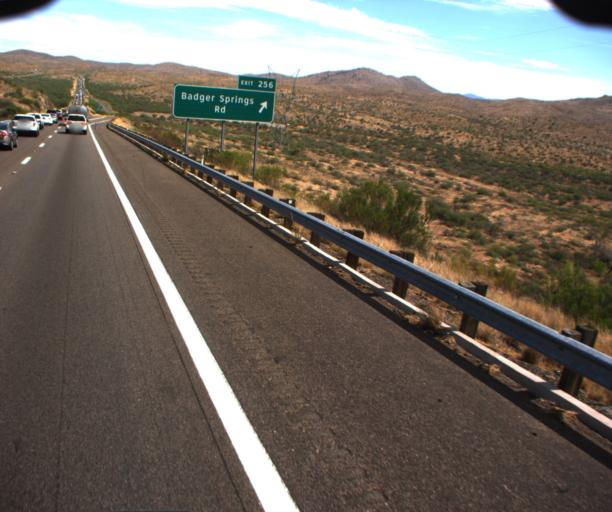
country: US
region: Arizona
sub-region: Yavapai County
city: Cordes Lakes
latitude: 34.2315
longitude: -112.1113
